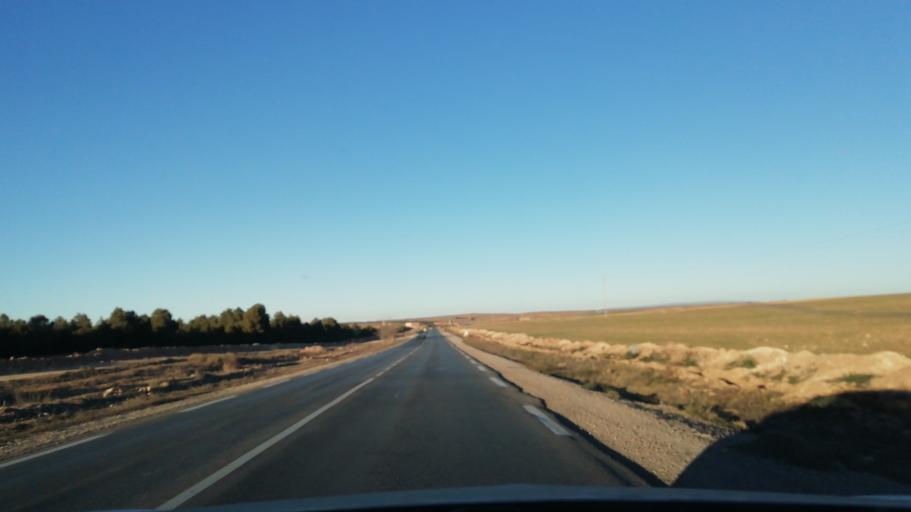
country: DZ
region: Saida
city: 'Ain el Hadjar
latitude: 34.5647
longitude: 0.1210
